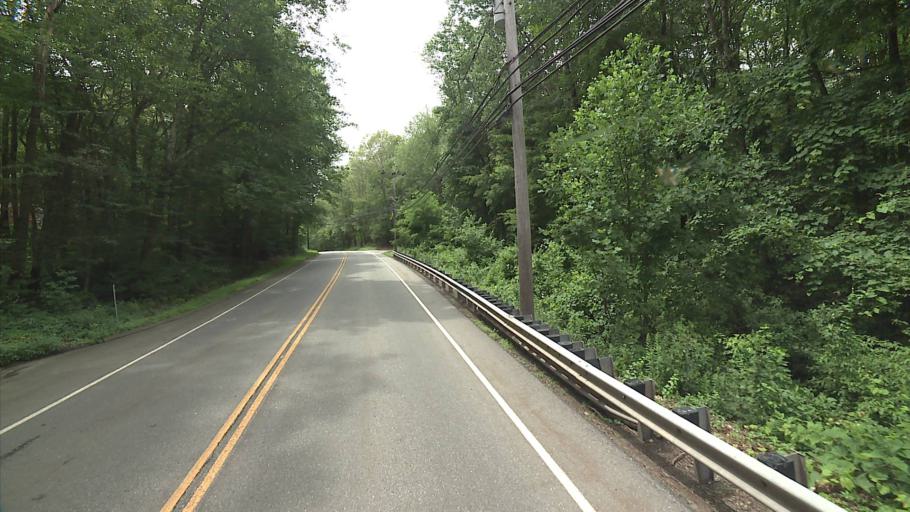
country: US
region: Connecticut
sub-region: New Haven County
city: Guilford
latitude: 41.3572
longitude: -72.6496
